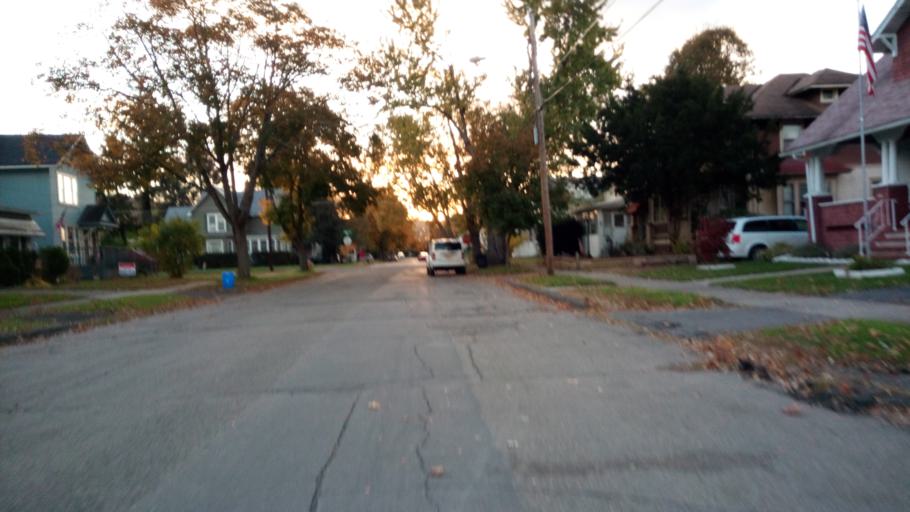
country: US
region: New York
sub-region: Chemung County
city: Elmira
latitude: 42.0763
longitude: -76.8138
